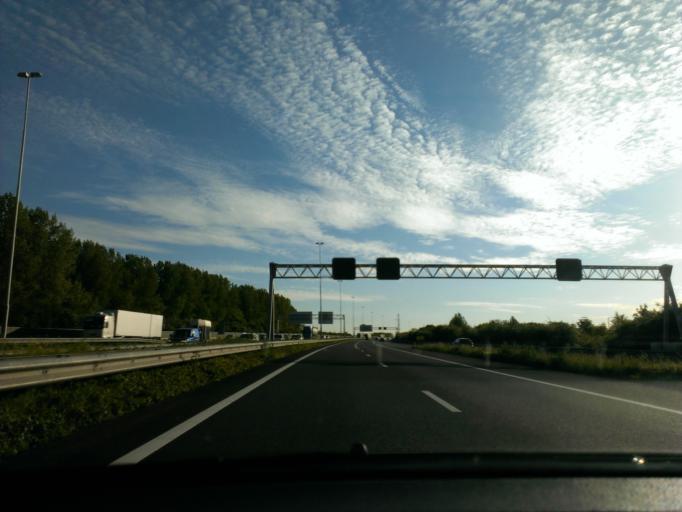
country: NL
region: South Holland
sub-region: Gemeente Gorinchem
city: Gorinchem
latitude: 51.8416
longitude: 4.9364
